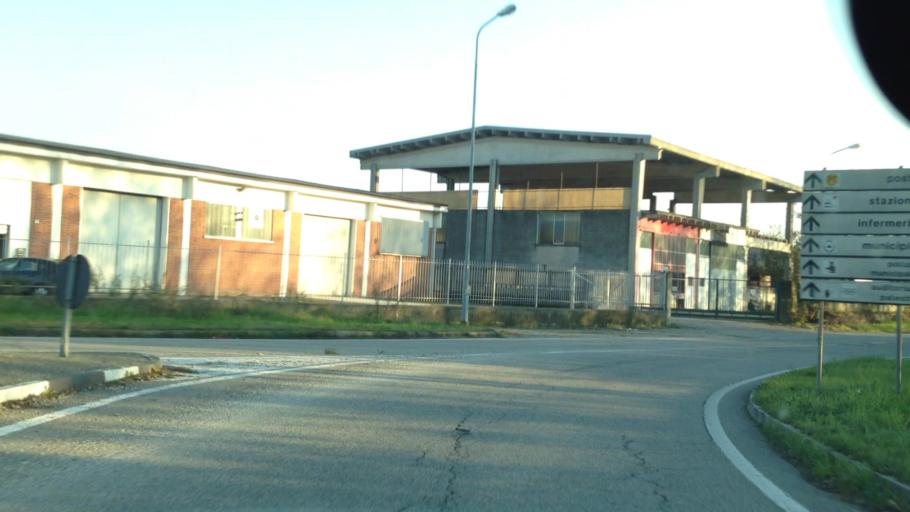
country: IT
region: Piedmont
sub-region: Provincia di Vercelli
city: Crescentino
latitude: 45.1977
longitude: 8.1037
